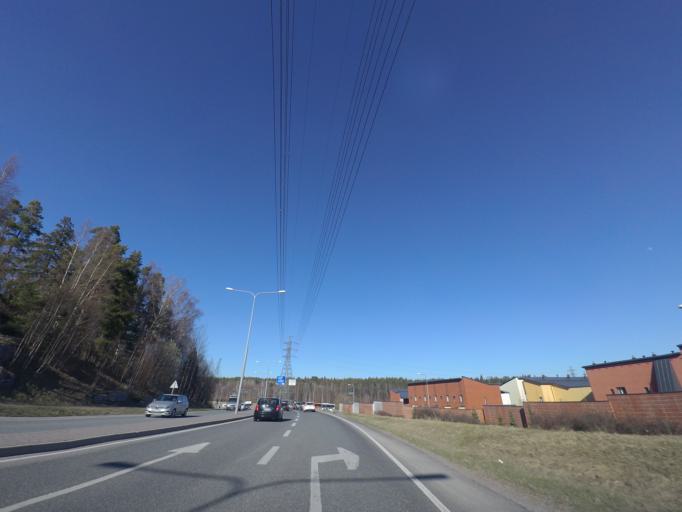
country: FI
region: Uusimaa
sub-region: Helsinki
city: Vantaa
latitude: 60.2318
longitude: 25.1307
